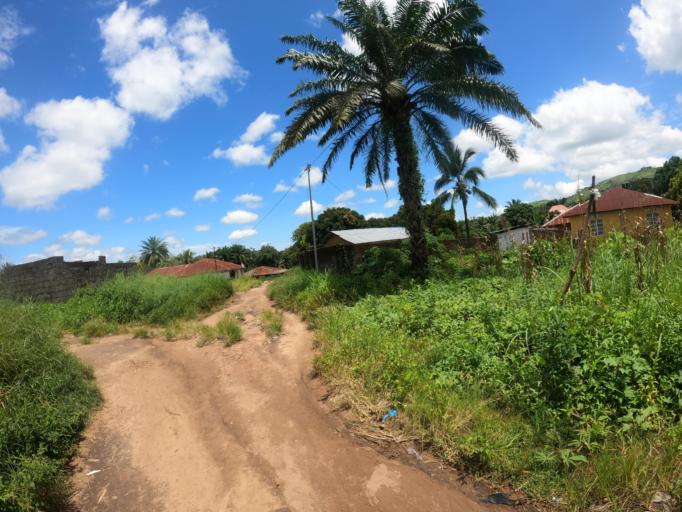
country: SL
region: Northern Province
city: Makeni
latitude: 8.8958
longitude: -12.0629
